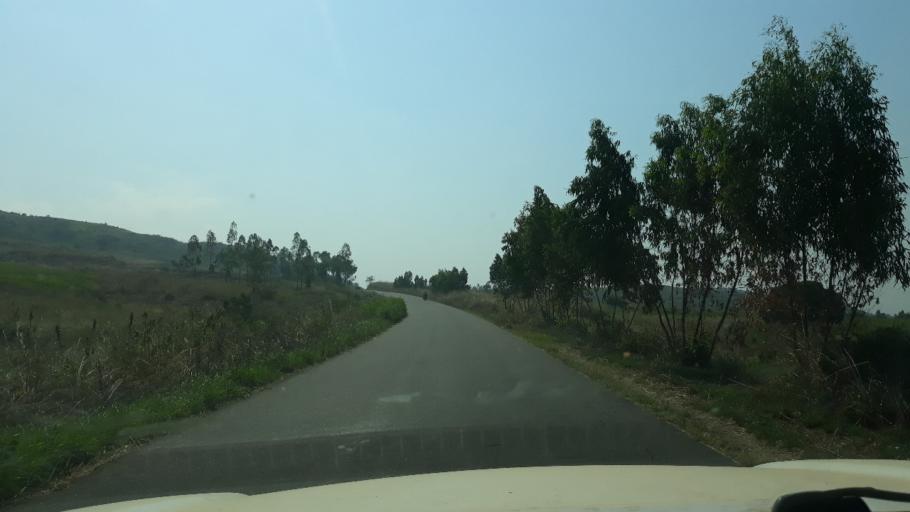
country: CD
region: South Kivu
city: Uvira
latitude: -3.2062
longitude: 29.1627
